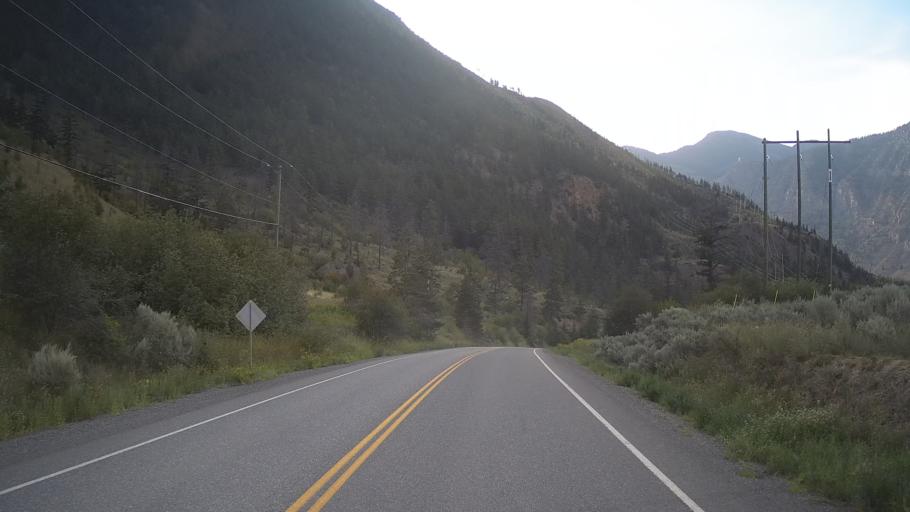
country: CA
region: British Columbia
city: Lillooet
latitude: 50.7439
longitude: -121.8884
